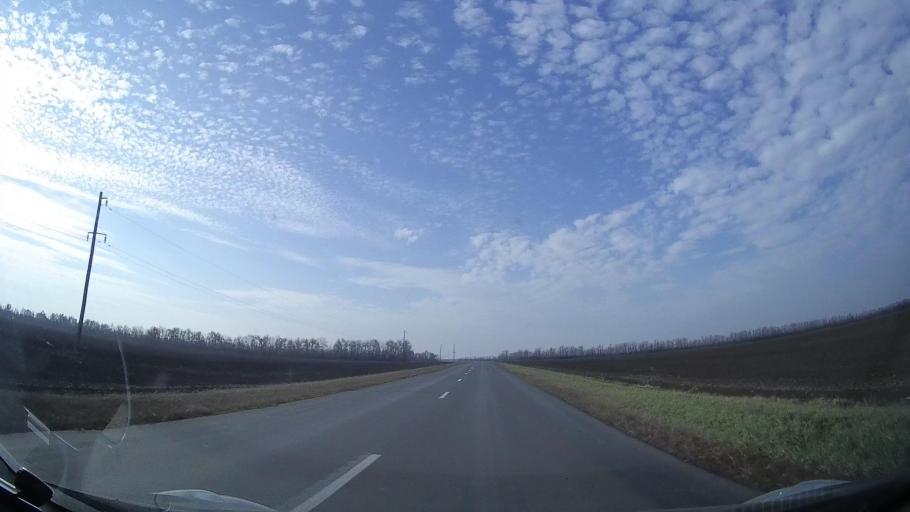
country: RU
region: Rostov
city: Veselyy
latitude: 46.9696
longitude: 40.6574
